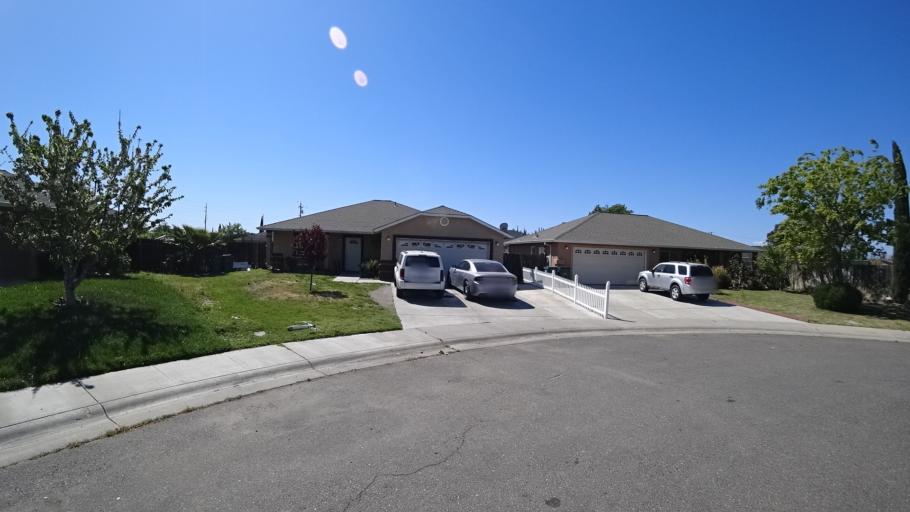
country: US
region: California
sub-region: Glenn County
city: Orland
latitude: 39.7554
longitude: -122.1982
